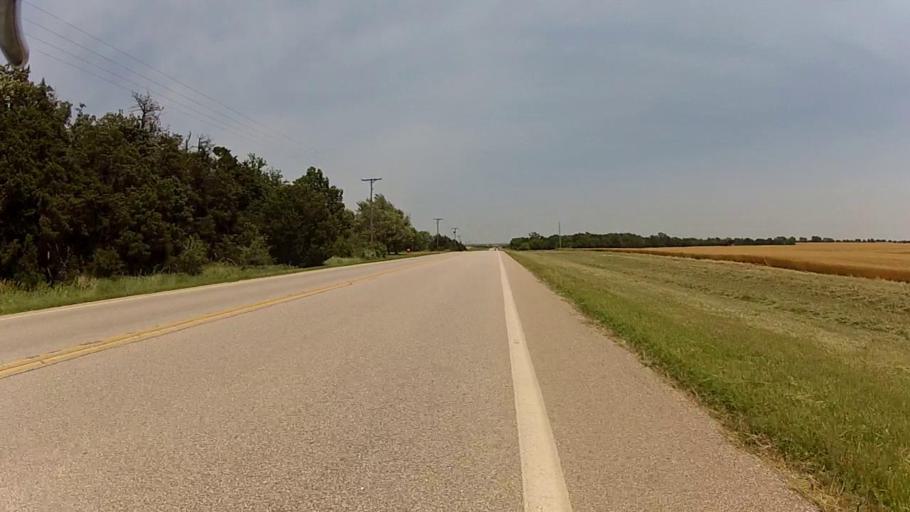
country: US
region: Kansas
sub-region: Cowley County
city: Arkansas City
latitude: 37.0568
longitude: -97.1586
